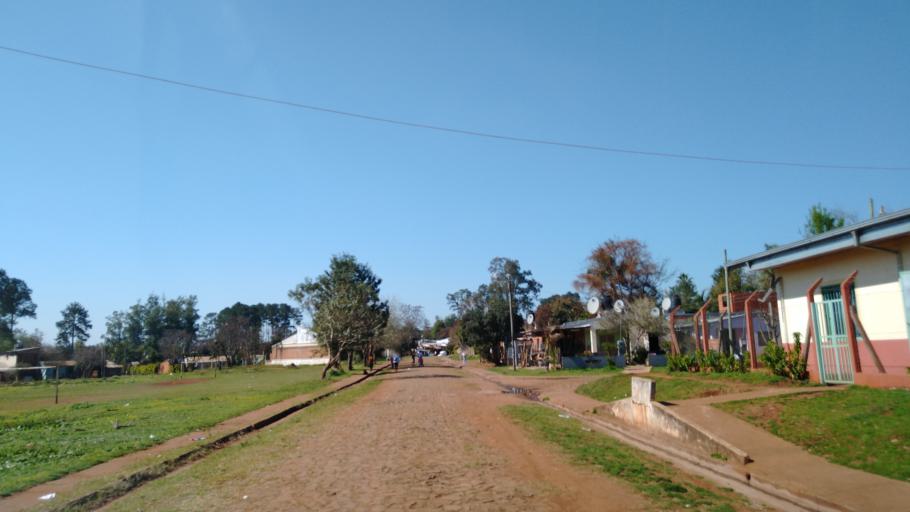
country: AR
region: Misiones
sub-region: Departamento de Capital
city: Posadas
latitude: -27.4182
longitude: -55.9617
